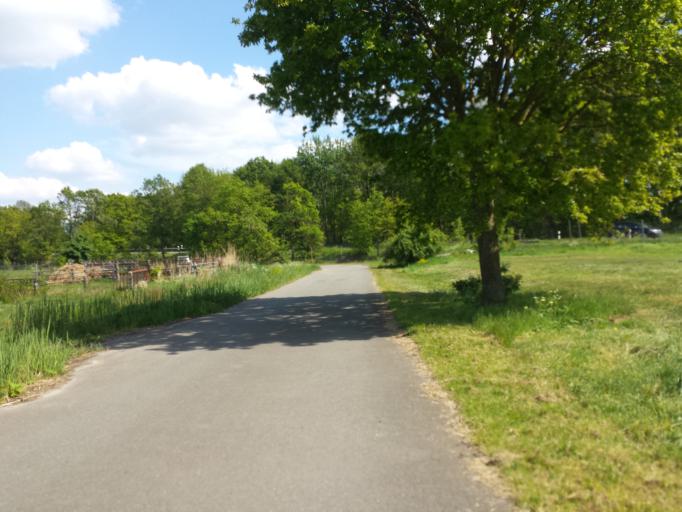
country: DE
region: Lower Saxony
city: Lilienthal
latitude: 53.1123
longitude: 8.8647
